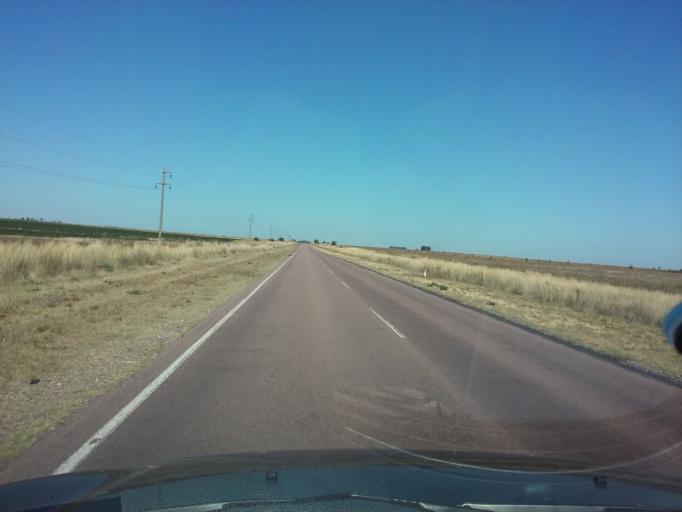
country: AR
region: La Pampa
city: Colonia Baron
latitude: -36.2101
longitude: -63.9429
